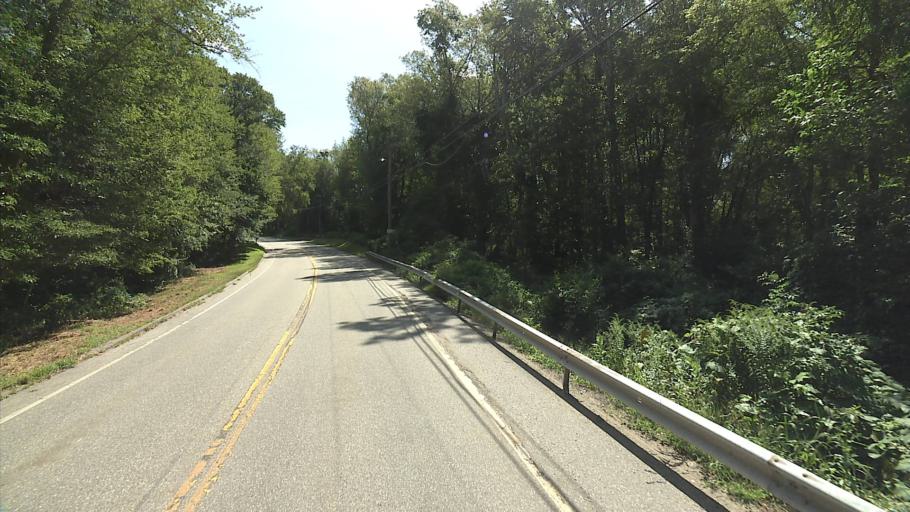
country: US
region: Rhode Island
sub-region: Washington County
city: Hopkinton
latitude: 41.5620
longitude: -71.8217
